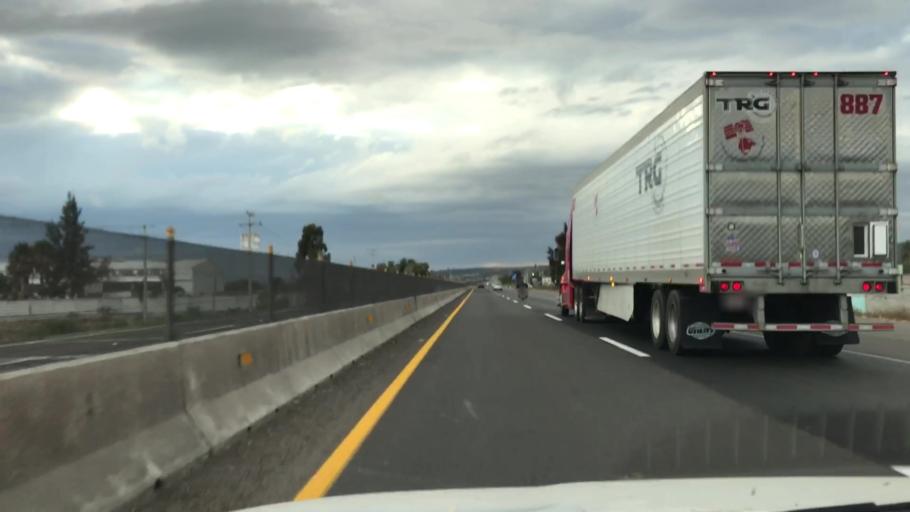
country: MX
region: Guanajuato
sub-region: Penjamo
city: Estacion la Piedad
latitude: 20.3885
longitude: -101.9391
